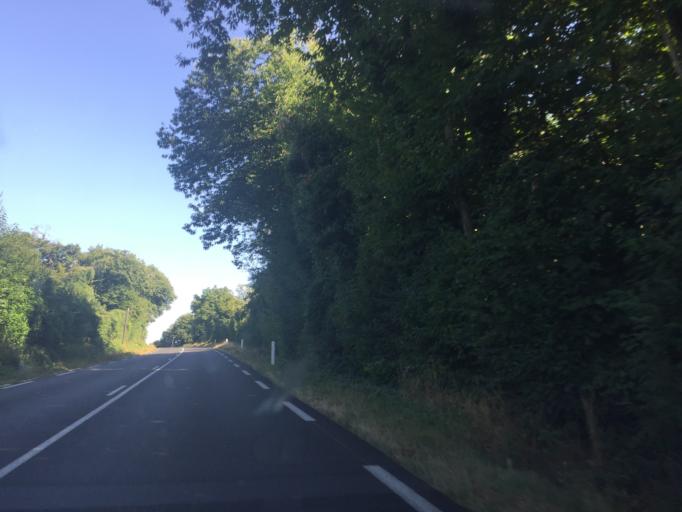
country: FR
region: Poitou-Charentes
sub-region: Departement des Deux-Sevres
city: Melle
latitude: 46.2096
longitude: -0.1090
